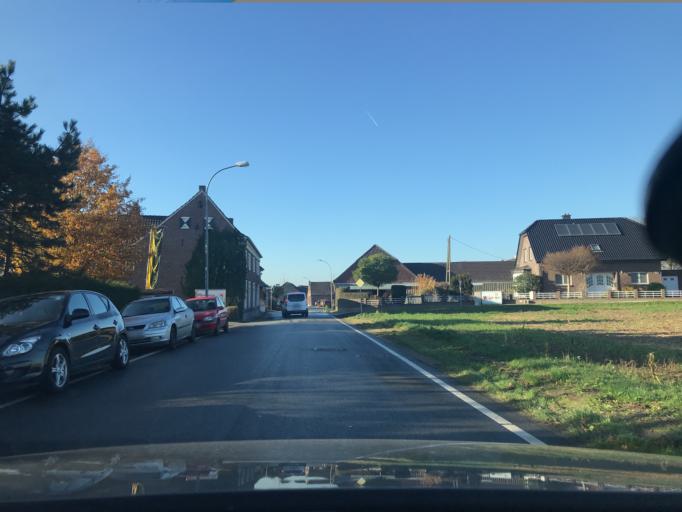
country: DE
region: North Rhine-Westphalia
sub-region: Regierungsbezirk Dusseldorf
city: Rheurdt
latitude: 51.4341
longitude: 6.4056
